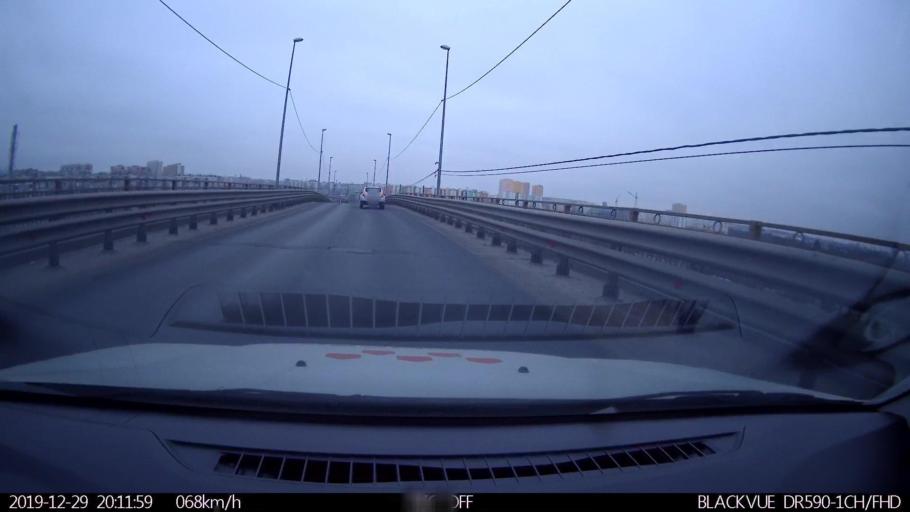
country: RU
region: Nizjnij Novgorod
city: Nizhniy Novgorod
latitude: 56.3507
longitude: 43.9227
